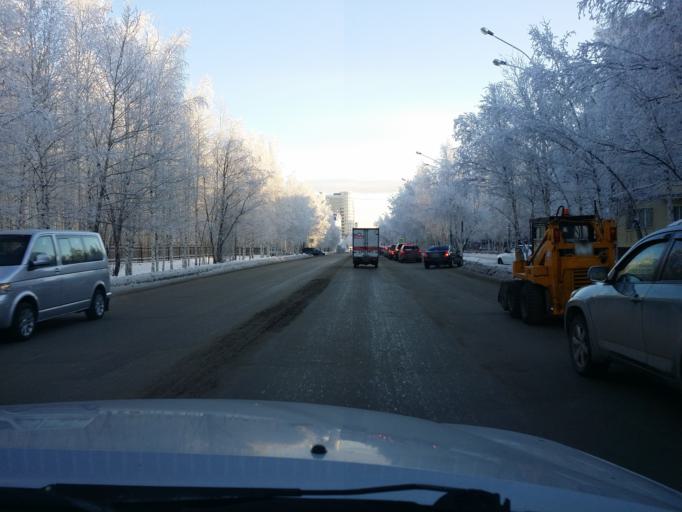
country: RU
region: Khanty-Mansiyskiy Avtonomnyy Okrug
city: Nizhnevartovsk
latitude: 60.9374
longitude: 76.5689
